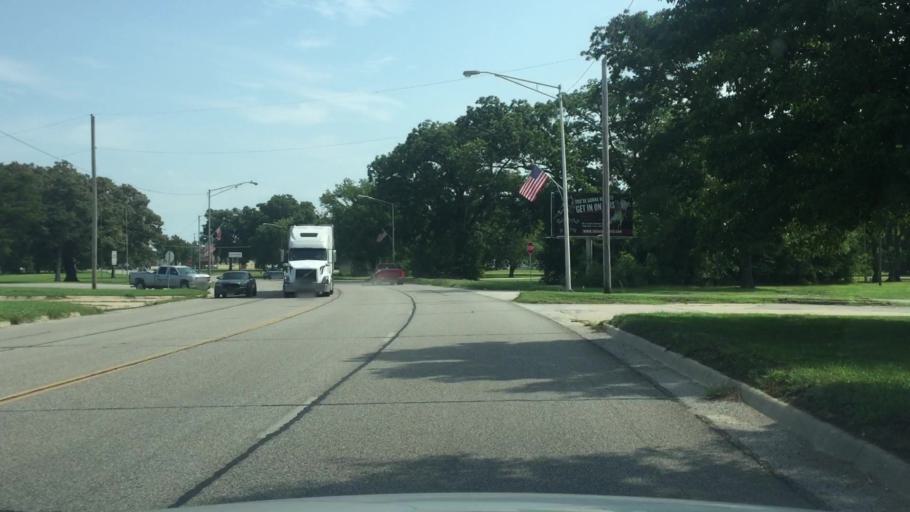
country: US
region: Kansas
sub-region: Montgomery County
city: Coffeyville
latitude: 37.0332
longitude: -95.6024
